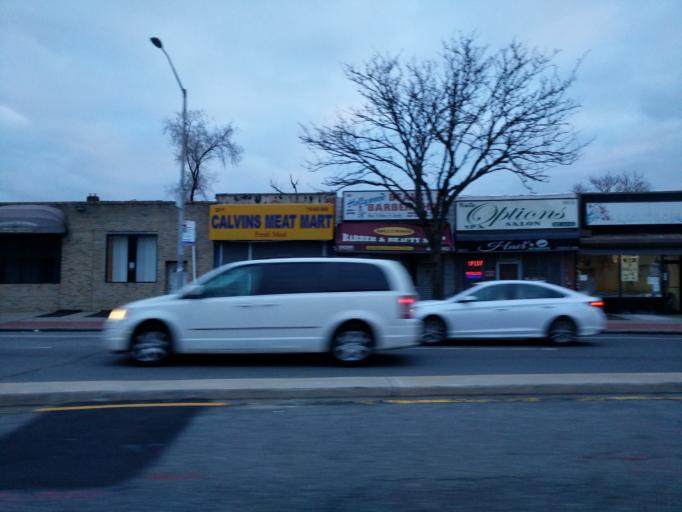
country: US
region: New York
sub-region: Nassau County
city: South Valley Stream
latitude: 40.6772
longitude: -73.7435
